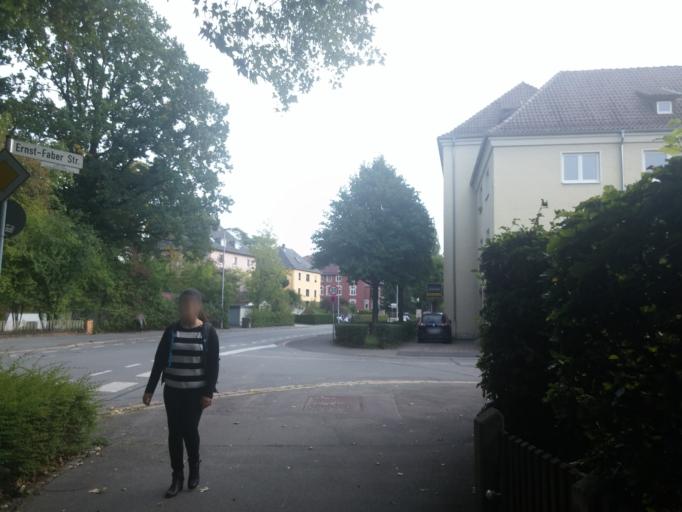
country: DE
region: Bavaria
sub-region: Upper Franconia
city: Coburg
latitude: 50.2495
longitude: 10.9691
